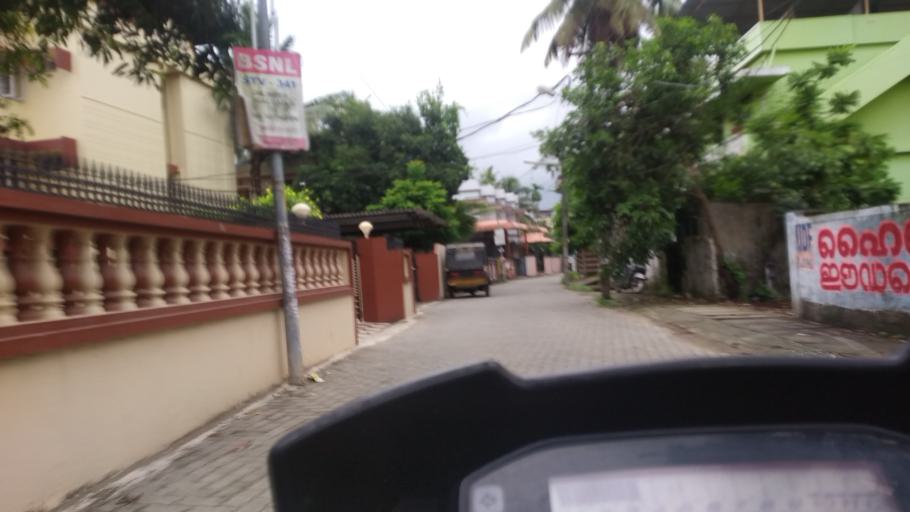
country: IN
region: Kerala
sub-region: Ernakulam
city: Cochin
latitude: 9.9819
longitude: 76.2951
